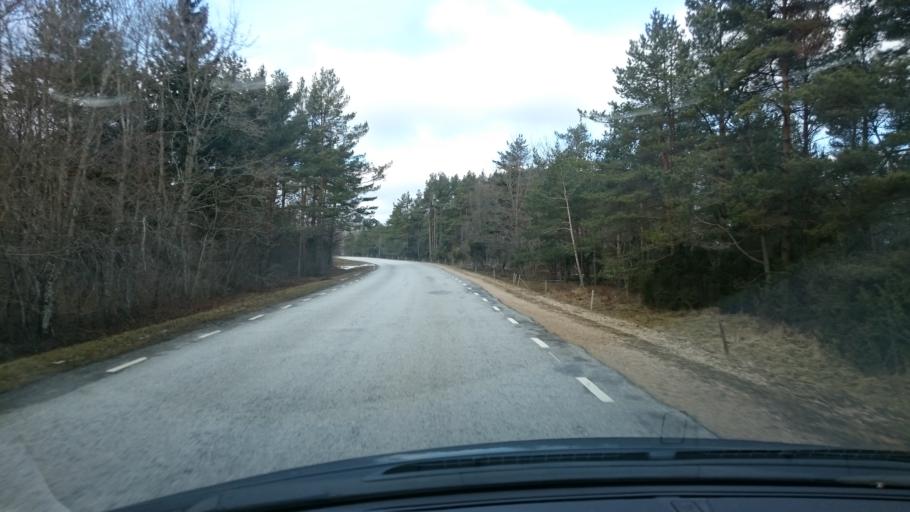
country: EE
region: Harju
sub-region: Keila linn
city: Keila
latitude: 59.3633
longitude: 24.3363
